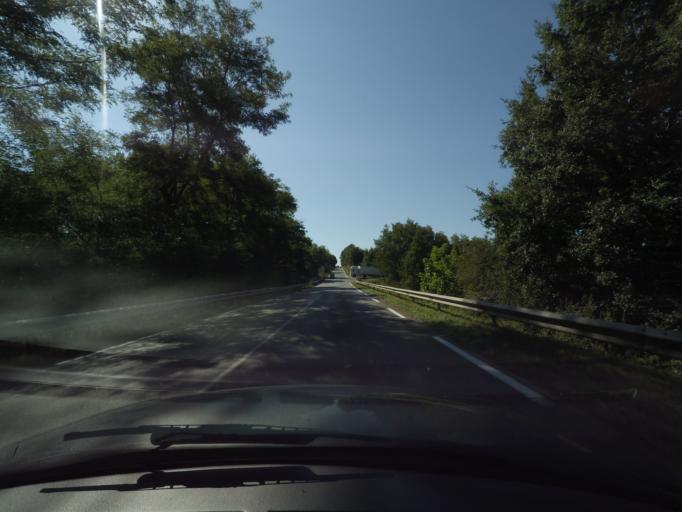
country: FR
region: Poitou-Charentes
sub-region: Departement de la Vienne
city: Saulge
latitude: 46.3261
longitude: 0.8169
